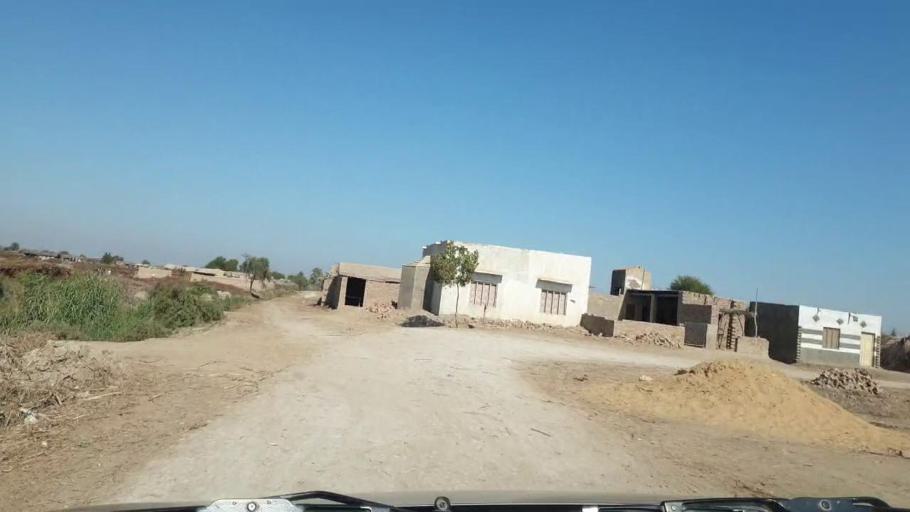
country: PK
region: Sindh
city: Sinjhoro
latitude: 26.1333
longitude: 68.8263
